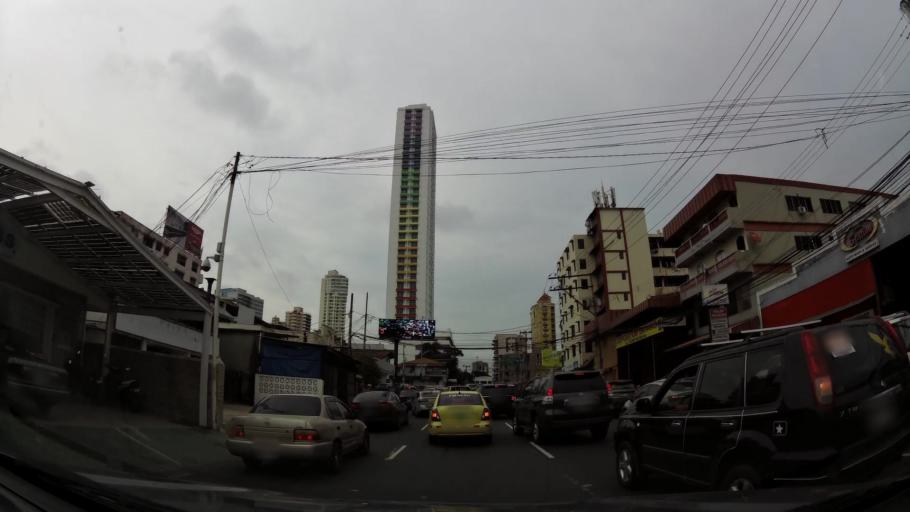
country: PA
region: Panama
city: Panama
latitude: 8.9930
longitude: -79.5191
